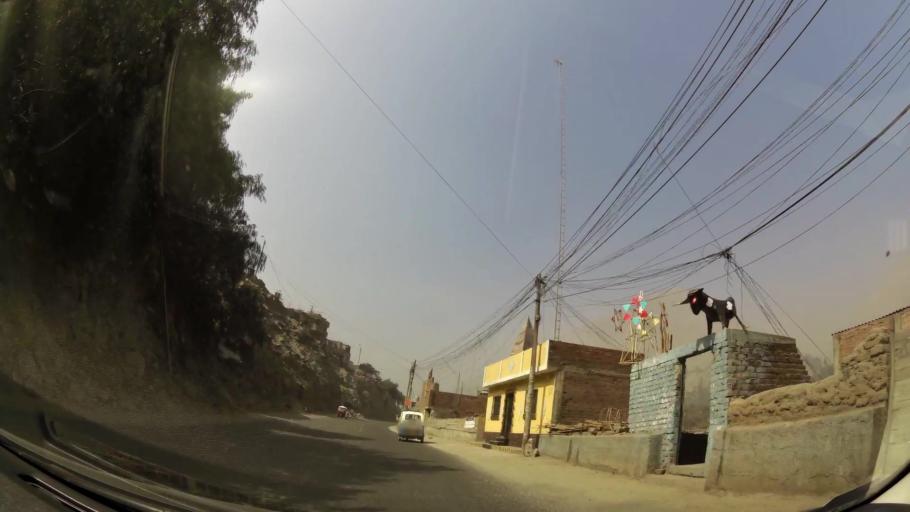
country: PE
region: Lima
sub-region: Provincia de Huarochiri
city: Ricardo Palma
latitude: -11.9239
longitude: -76.6820
